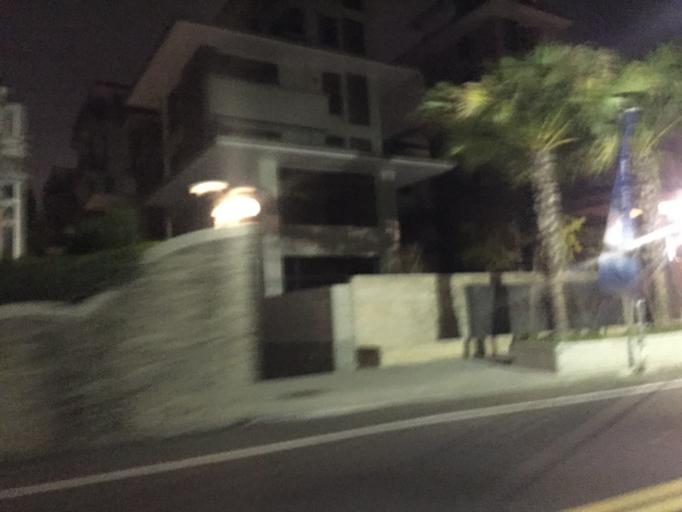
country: TW
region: Taiwan
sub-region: Hsinchu
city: Hsinchu
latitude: 24.7712
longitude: 120.9694
